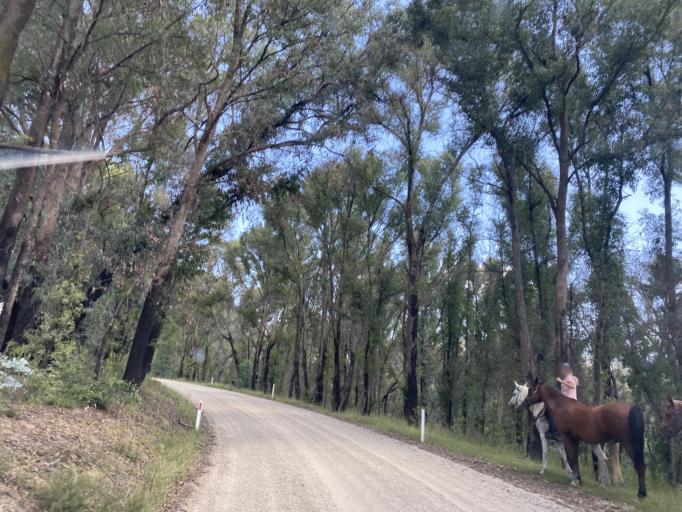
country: AU
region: Victoria
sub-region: Cardinia
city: Garfield
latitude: -37.9941
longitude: 145.6989
